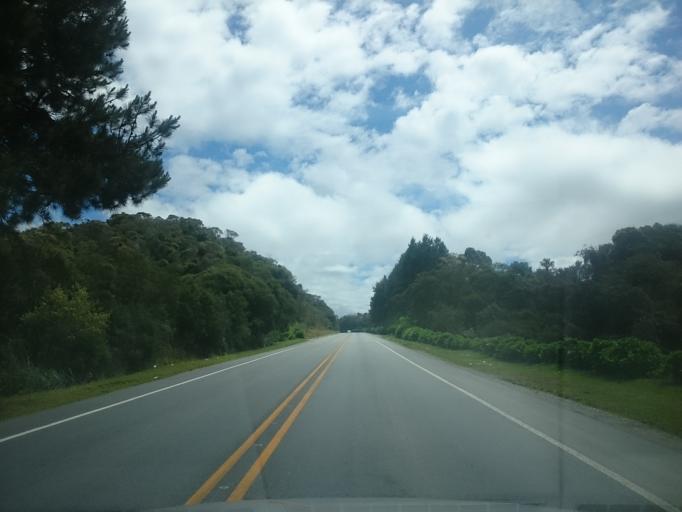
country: BR
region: Santa Catarina
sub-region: Anitapolis
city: Anitapolis
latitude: -27.6967
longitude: -49.0490
